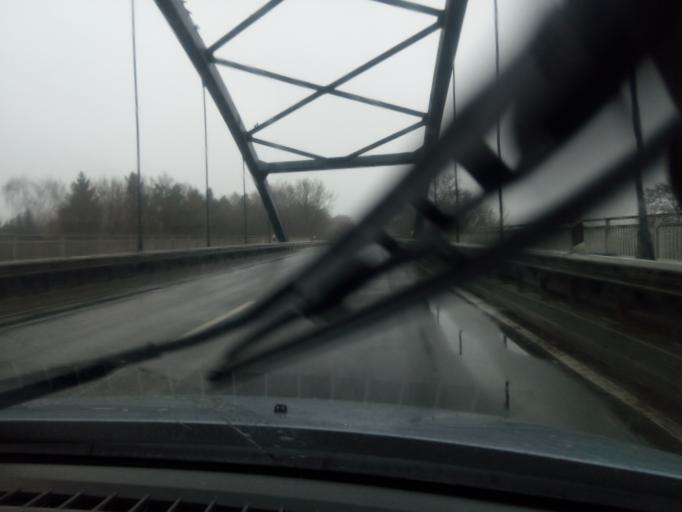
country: DE
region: Lower Saxony
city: Heede
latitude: 52.9801
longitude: 7.3024
